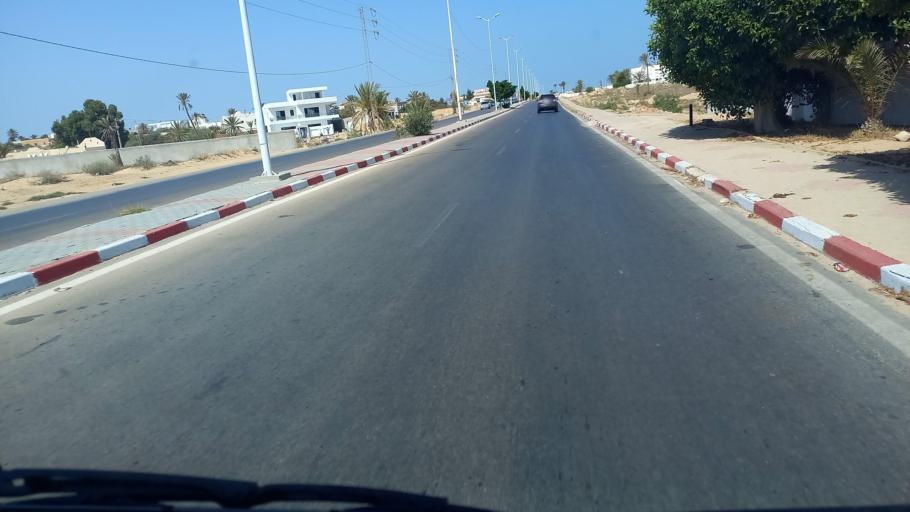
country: TN
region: Madanin
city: Midoun
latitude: 33.8603
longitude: 10.9709
